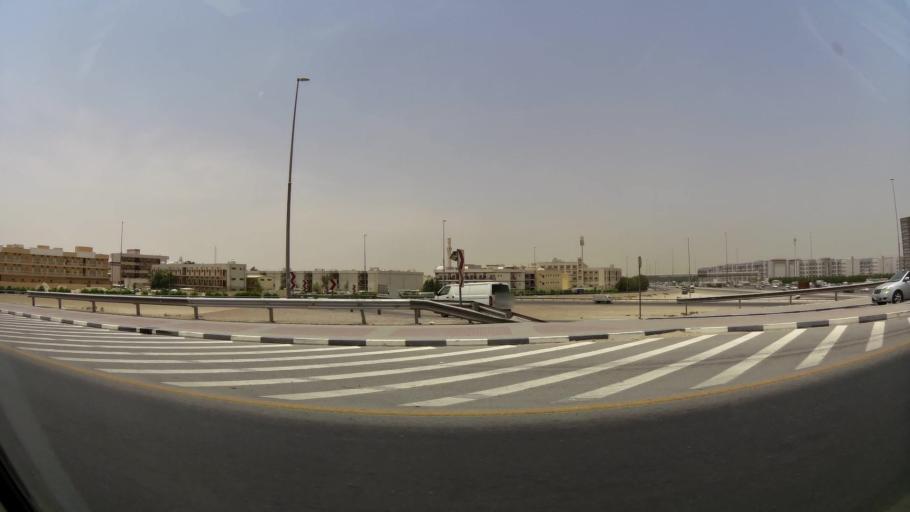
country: AE
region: Ash Shariqah
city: Sharjah
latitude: 25.2783
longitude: 55.4237
